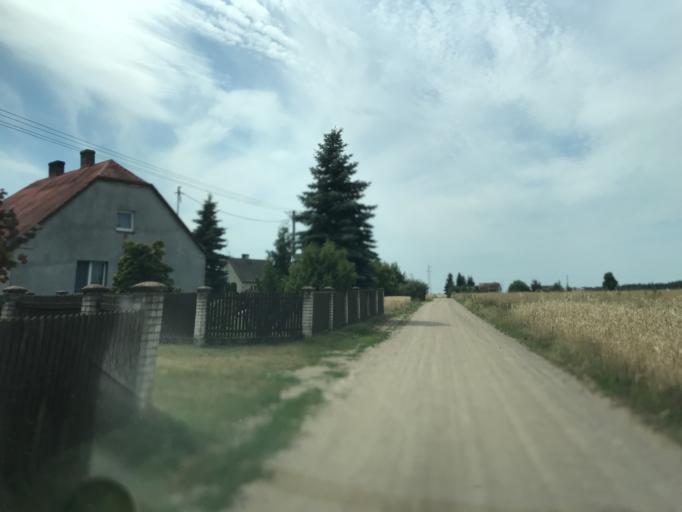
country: PL
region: Kujawsko-Pomorskie
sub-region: Powiat brodnicki
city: Bartniczka
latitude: 53.2581
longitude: 19.5686
